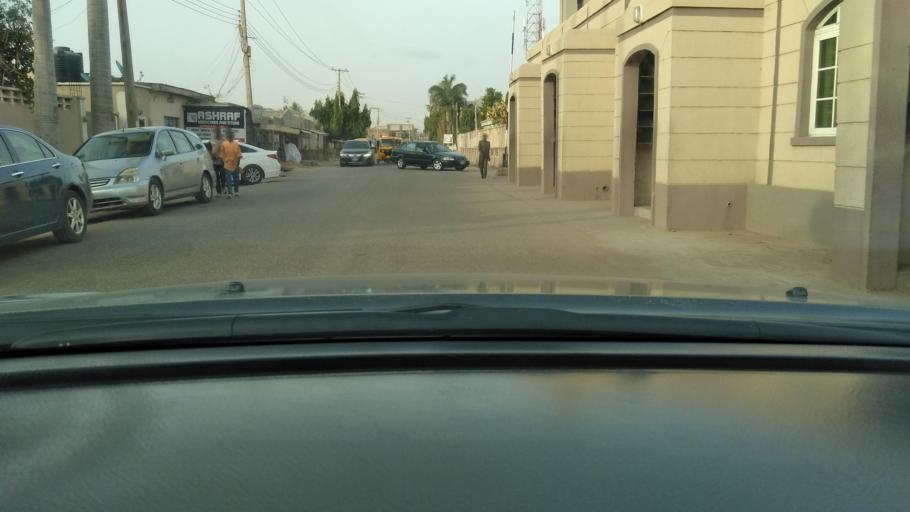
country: NG
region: Kano
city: Kano
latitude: 11.9578
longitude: 8.5224
